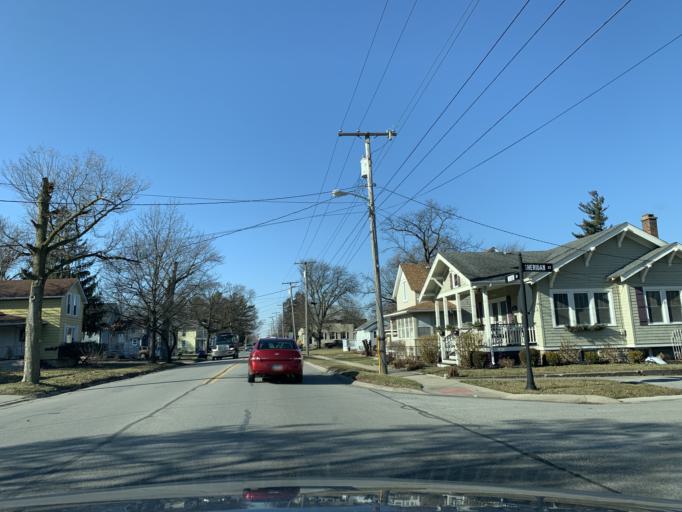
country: US
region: Indiana
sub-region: Lake County
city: Crown Point
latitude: 41.4203
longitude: -87.3583
